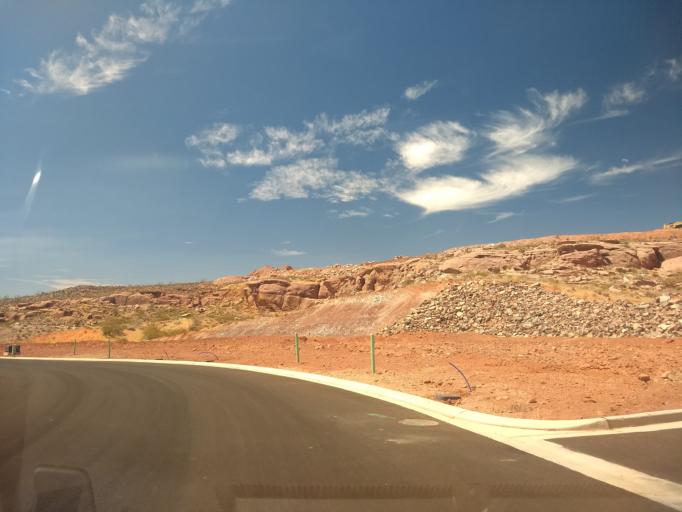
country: US
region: Utah
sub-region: Washington County
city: Washington
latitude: 37.1483
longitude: -113.4691
